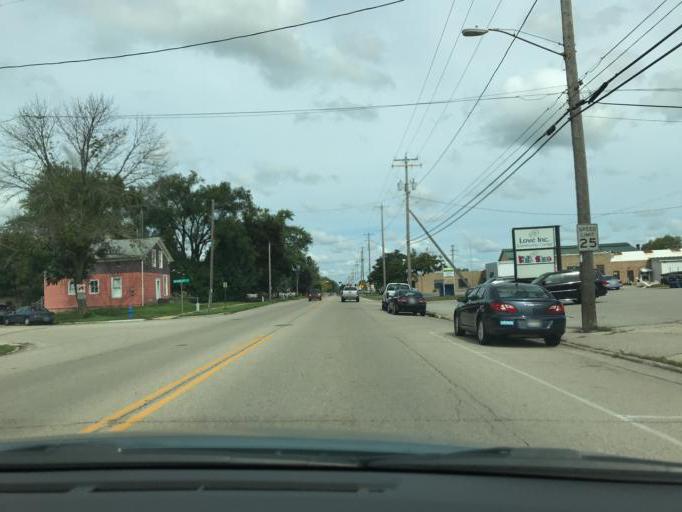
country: US
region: Wisconsin
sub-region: Racine County
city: Burlington
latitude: 42.6696
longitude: -88.2682
